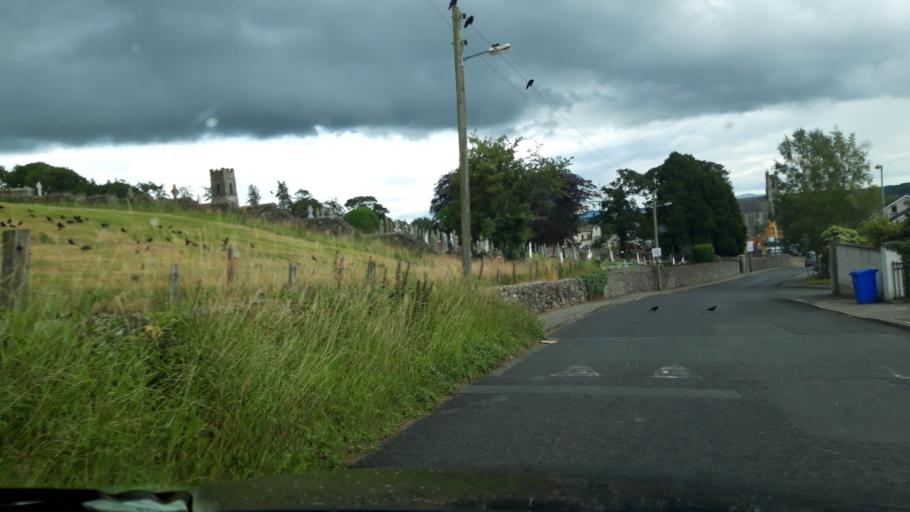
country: IE
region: Leinster
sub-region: Wicklow
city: Baltinglass
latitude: 52.9432
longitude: -6.7055
